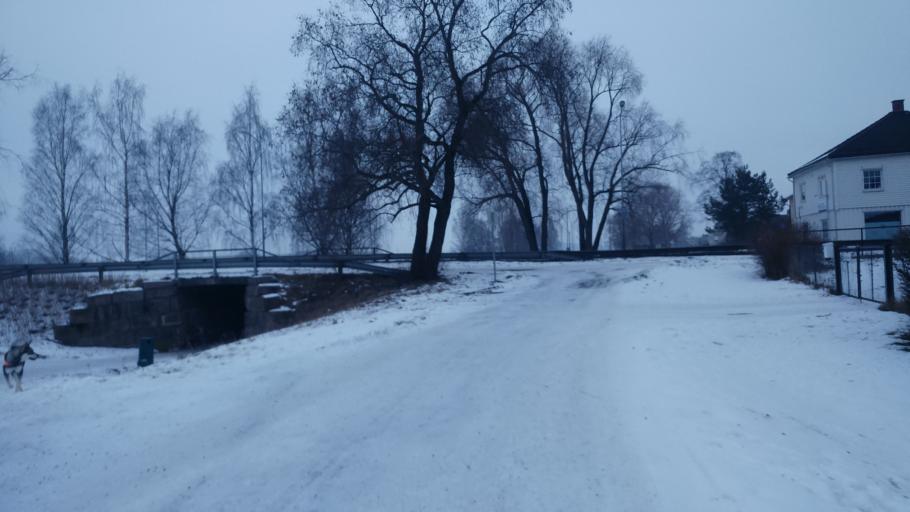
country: NO
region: Akershus
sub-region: Skedsmo
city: Lillestrom
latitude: 59.9568
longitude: 11.0308
